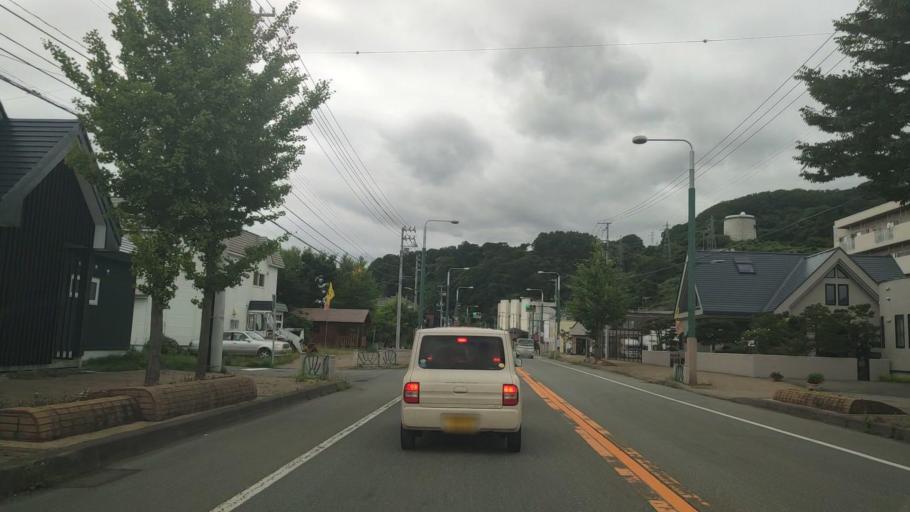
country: JP
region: Hokkaido
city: Date
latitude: 42.5514
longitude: 140.7617
